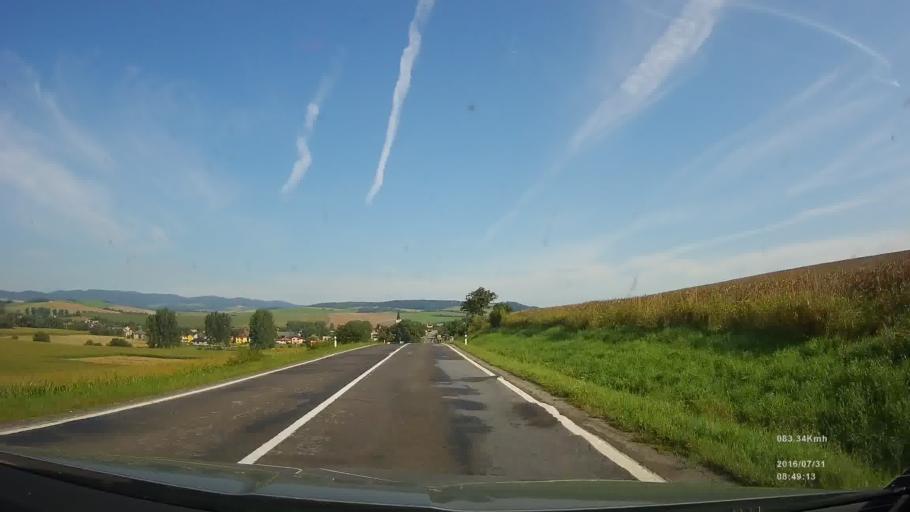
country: SK
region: Presovsky
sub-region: Okres Presov
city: Presov
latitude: 49.0823
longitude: 21.3167
